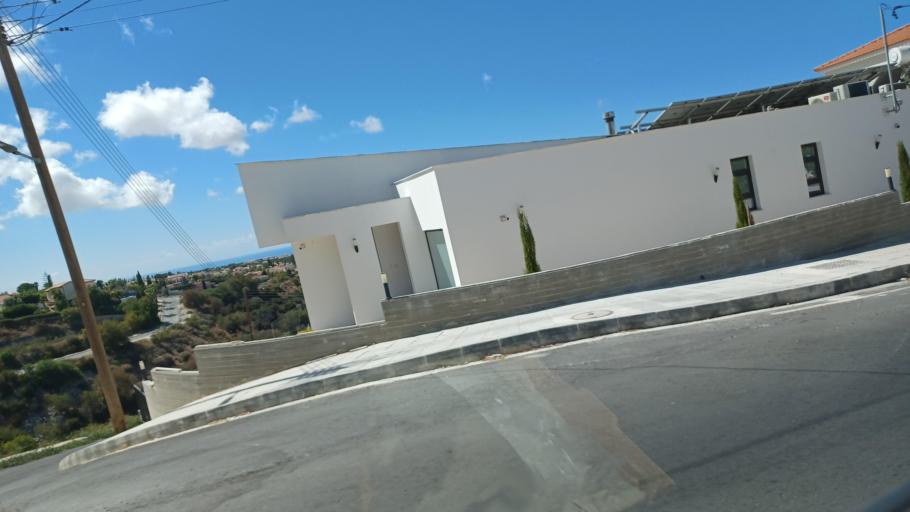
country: CY
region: Pafos
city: Tala
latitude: 34.8387
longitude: 32.4376
